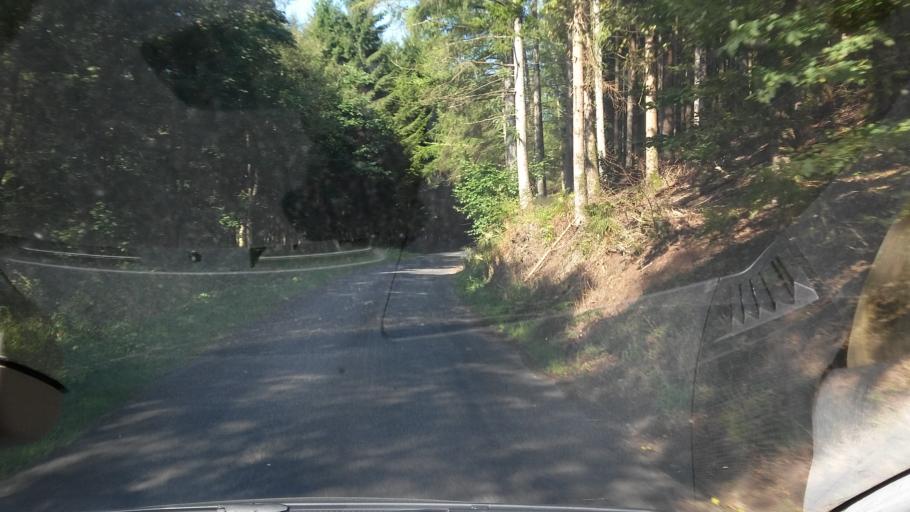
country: LU
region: Luxembourg
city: Eischen
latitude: 49.6975
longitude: 5.8598
